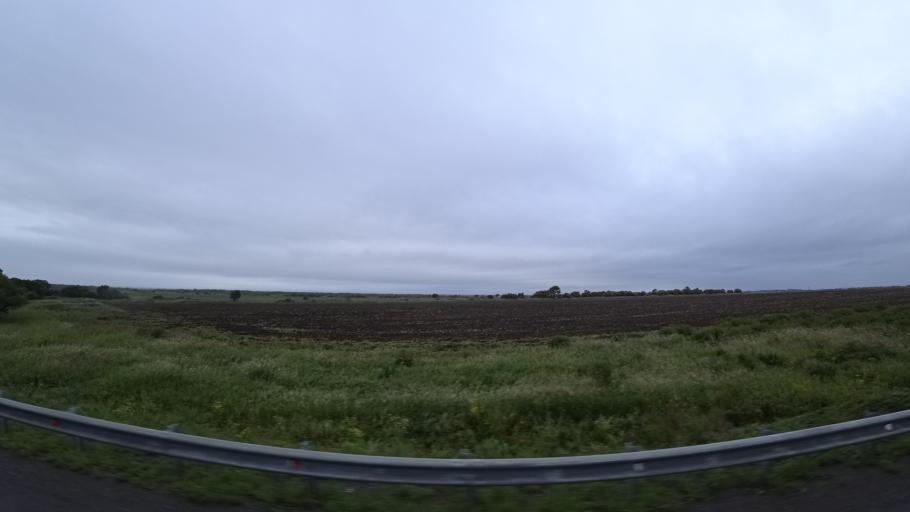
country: RU
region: Primorskiy
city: Chernigovka
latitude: 44.2943
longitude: 132.5153
